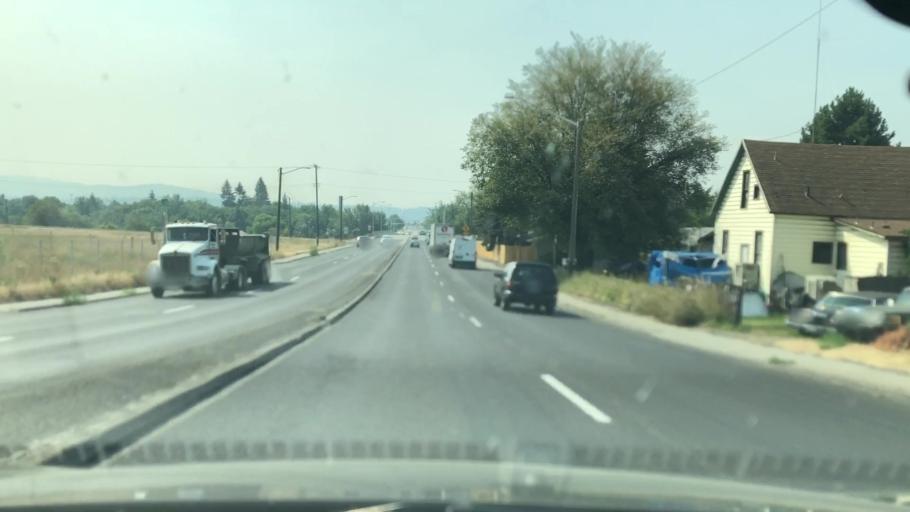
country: US
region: Washington
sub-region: Spokane County
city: Spokane
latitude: 47.6810
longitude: -117.3637
